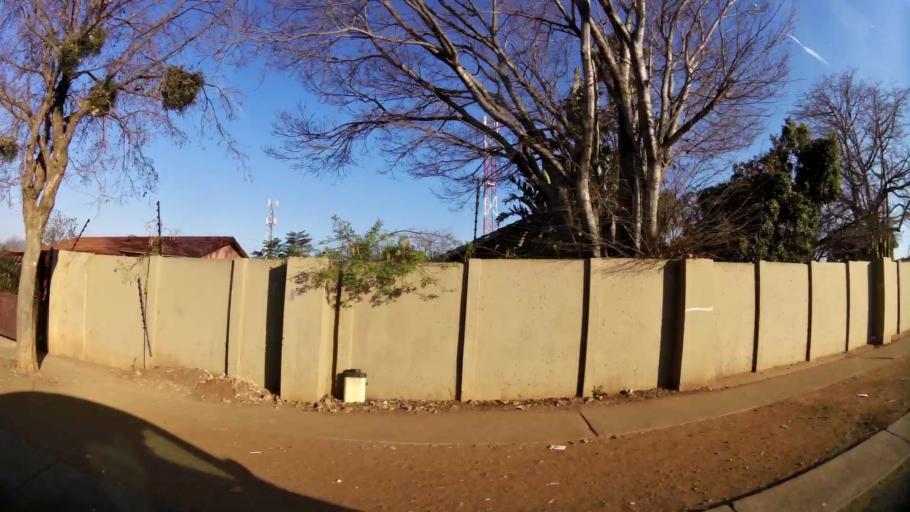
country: ZA
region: Gauteng
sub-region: City of Tshwane Metropolitan Municipality
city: Pretoria
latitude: -25.7422
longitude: 28.1216
